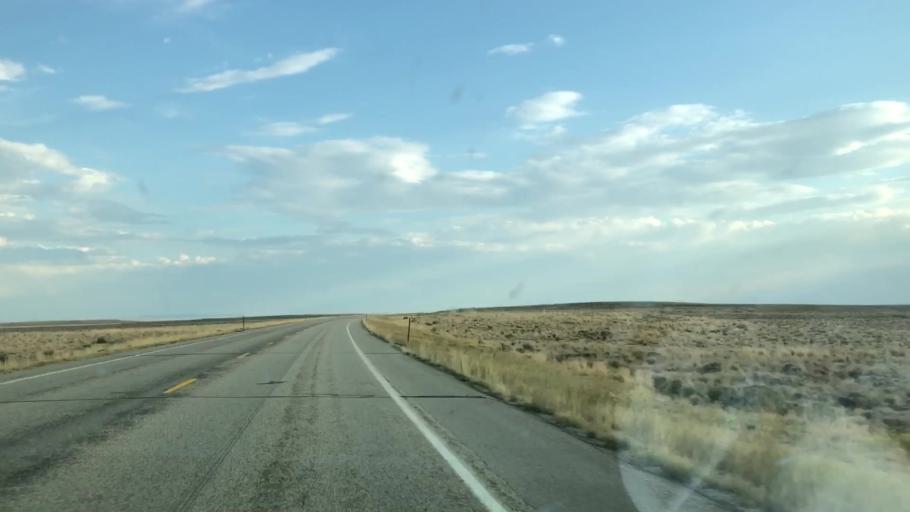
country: US
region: Wyoming
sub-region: Sweetwater County
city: North Rock Springs
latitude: 42.2544
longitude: -109.4682
